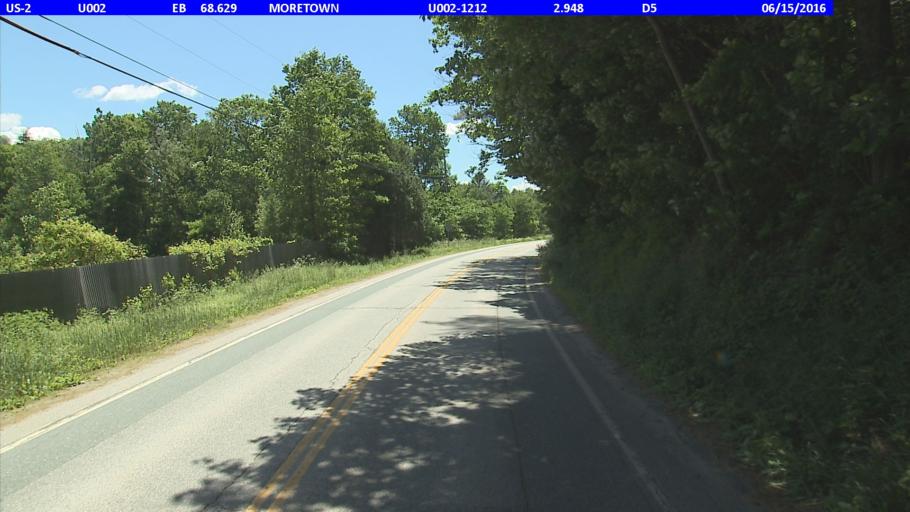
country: US
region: Vermont
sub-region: Washington County
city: Waterbury
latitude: 44.3100
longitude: -72.6978
